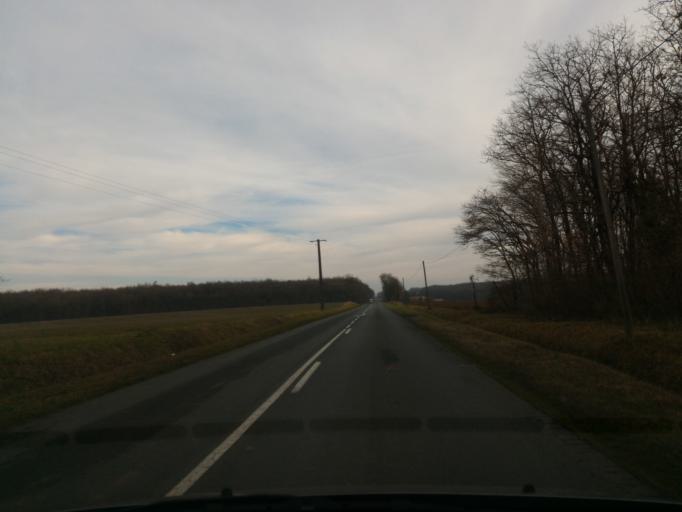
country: FR
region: Poitou-Charentes
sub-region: Departement de la Charente
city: Aigre
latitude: 45.9132
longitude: 0.0358
